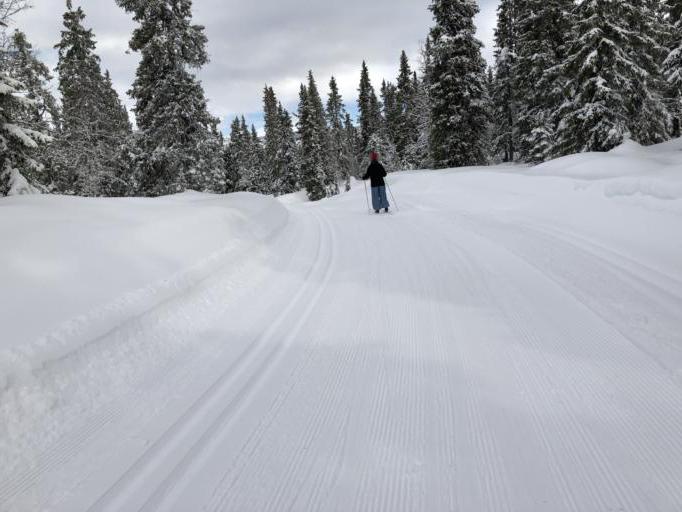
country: NO
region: Oppland
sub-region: Gausdal
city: Segalstad bru
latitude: 61.3259
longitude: 10.0782
